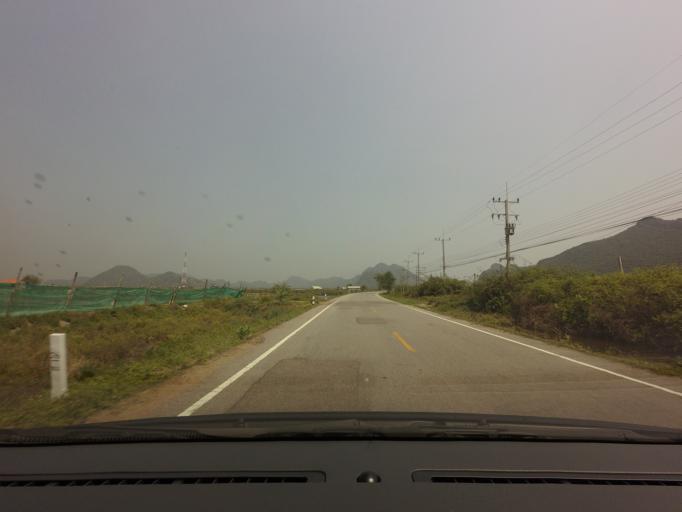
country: TH
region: Prachuap Khiri Khan
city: Kui Buri
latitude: 12.1645
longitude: 99.9852
